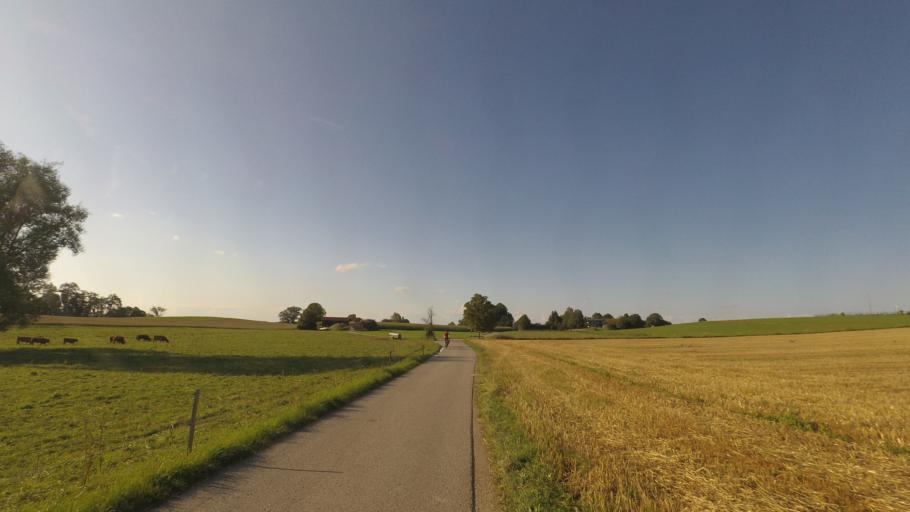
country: DE
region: Bavaria
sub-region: Upper Bavaria
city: Chieming
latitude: 47.8826
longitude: 12.5387
